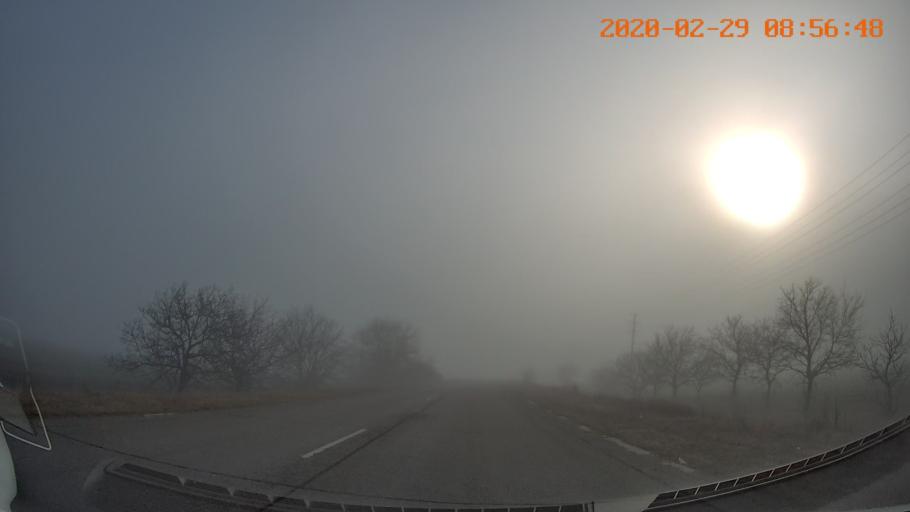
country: MD
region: Telenesti
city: Tiraspolul Nou
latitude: 46.9299
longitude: 29.6157
